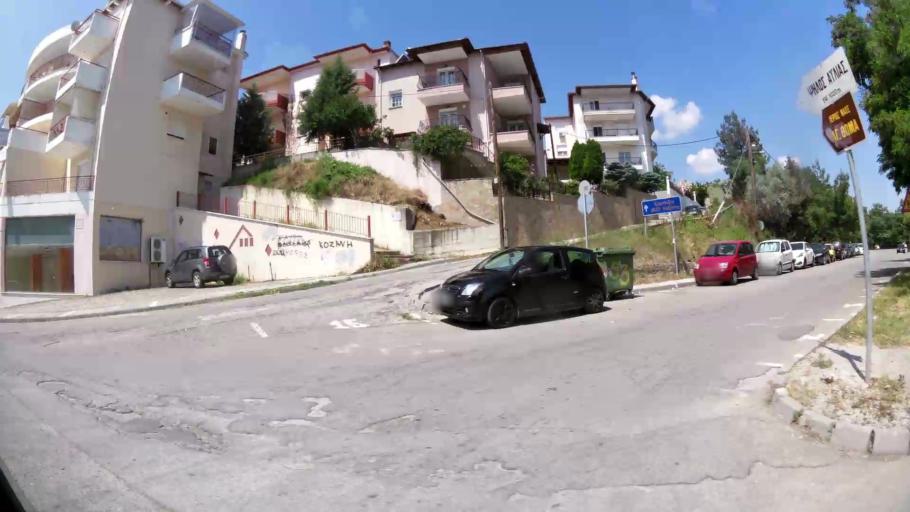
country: GR
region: West Macedonia
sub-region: Nomos Kozanis
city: Kozani
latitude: 40.3106
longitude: 21.7842
